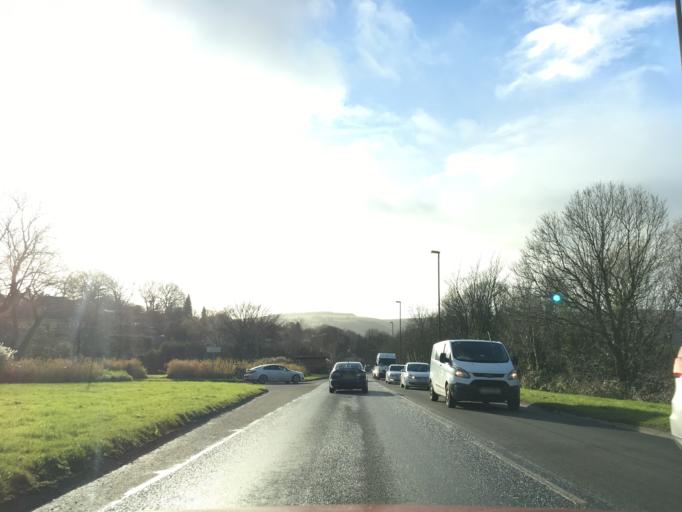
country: GB
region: Wales
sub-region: Caerphilly County Borough
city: Hengoed
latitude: 51.6439
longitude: -3.2234
